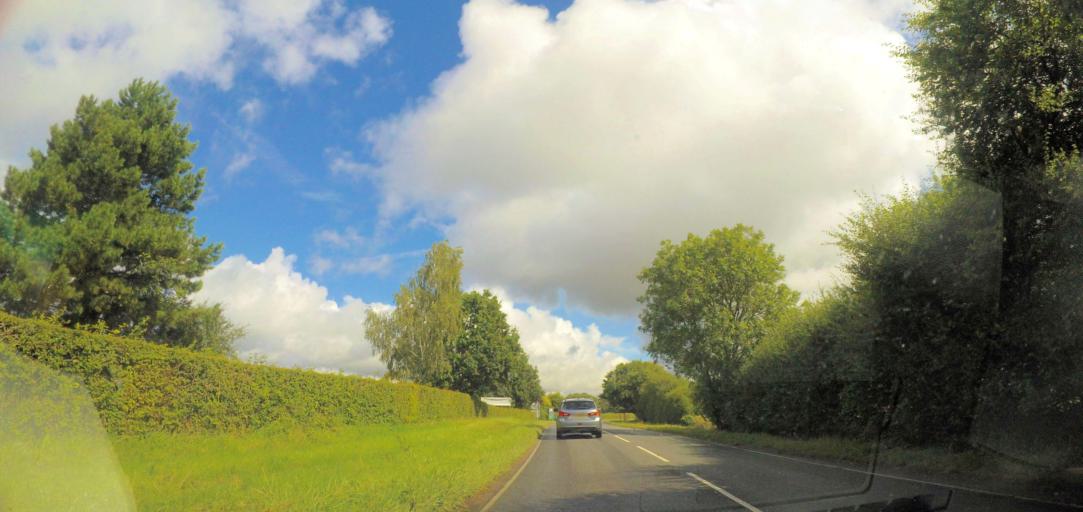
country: GB
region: England
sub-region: Hampshire
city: Bishopstoke
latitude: 50.9530
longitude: -1.3166
